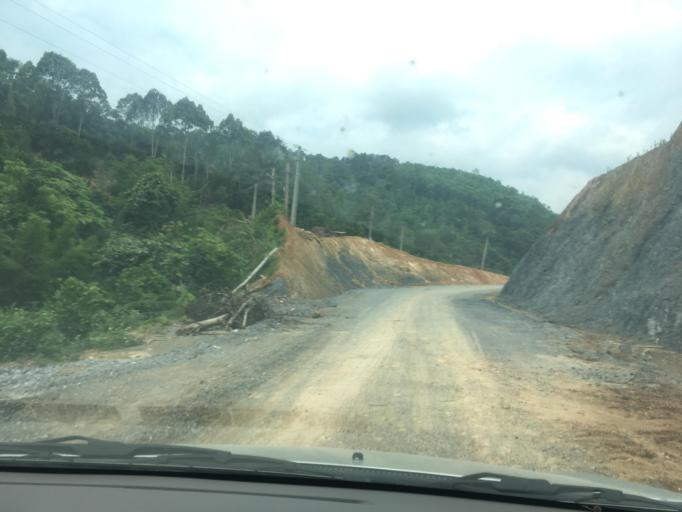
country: VN
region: Bac Kan
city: Yen Lac
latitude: 22.1665
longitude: 106.3010
